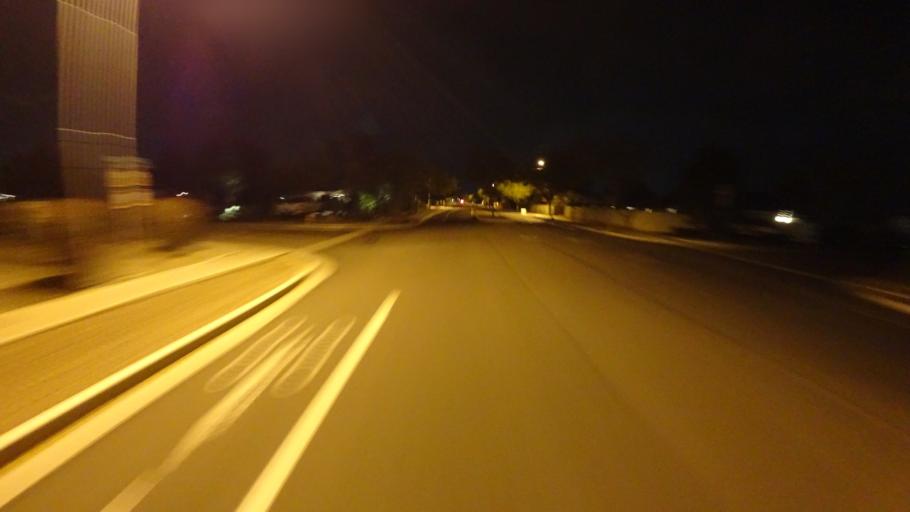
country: US
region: Arizona
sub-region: Maricopa County
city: Tempe Junction
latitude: 33.3990
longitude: -111.9349
